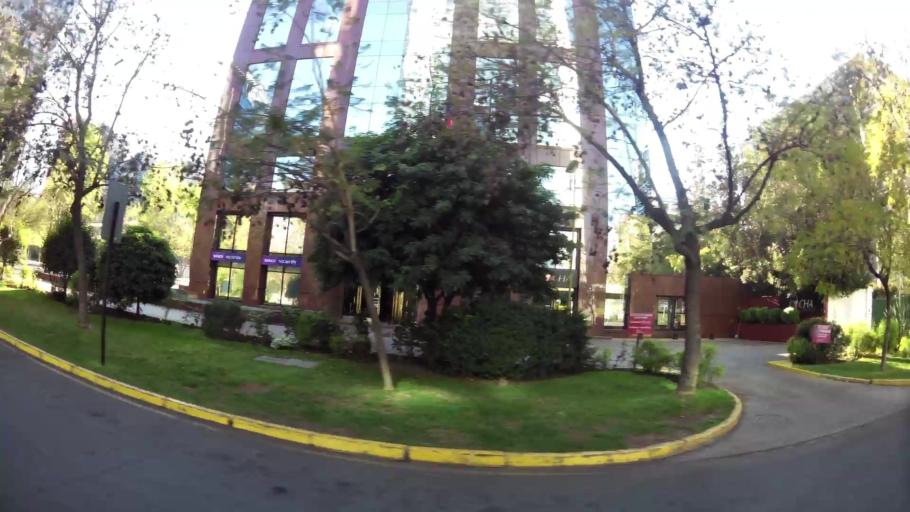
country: CL
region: Santiago Metropolitan
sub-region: Provincia de Santiago
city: Villa Presidente Frei, Nunoa, Santiago, Chile
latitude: -33.4157
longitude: -70.5895
